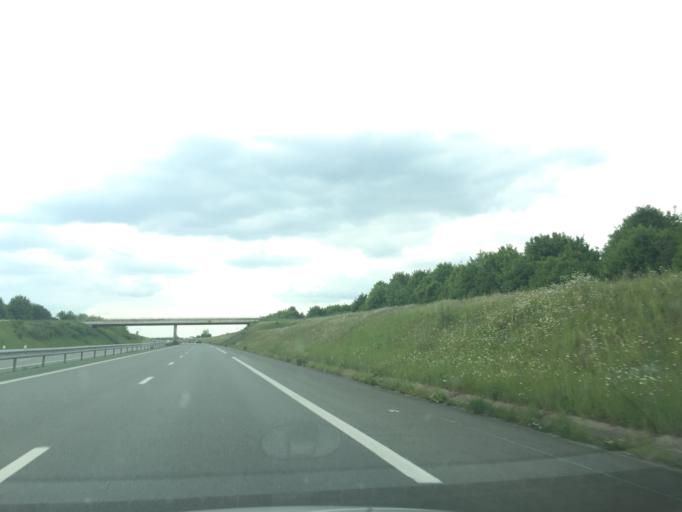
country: FR
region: Poitou-Charentes
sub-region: Departement des Deux-Sevres
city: Villiers-en-Plaine
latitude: 46.4210
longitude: -0.5545
